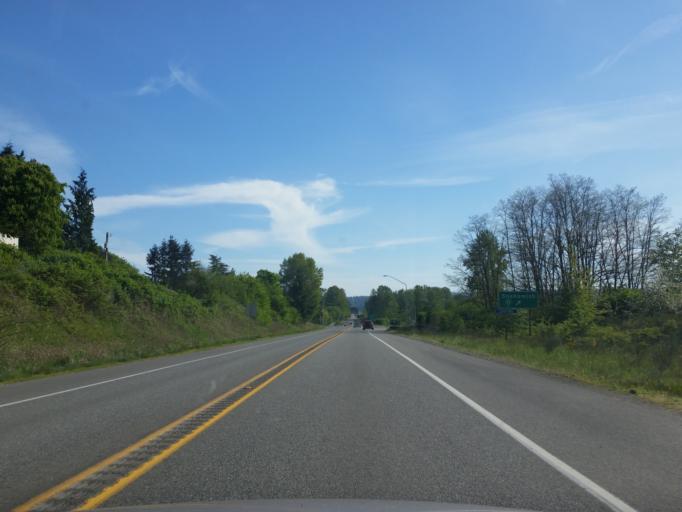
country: US
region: Washington
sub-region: Snohomish County
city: Snohomish
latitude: 47.9208
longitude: -122.1084
